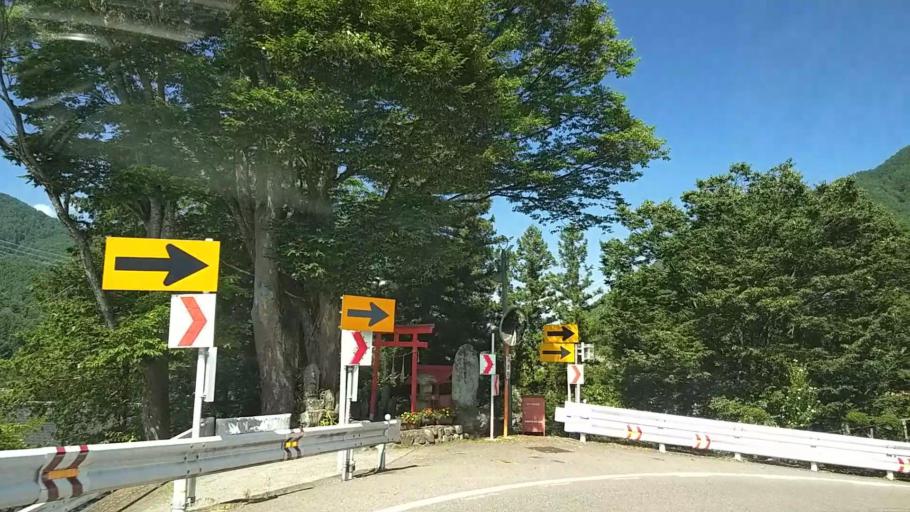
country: JP
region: Nagano
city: Matsumoto
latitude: 36.2178
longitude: 138.0488
